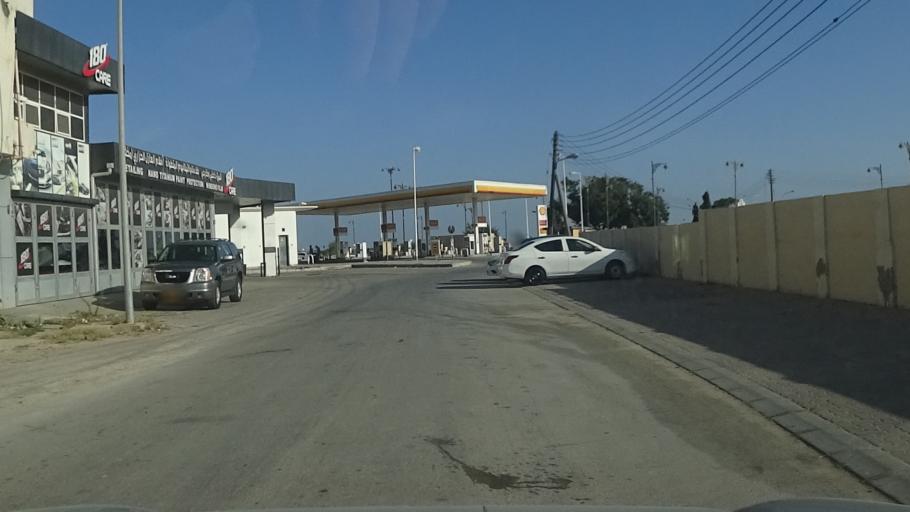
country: OM
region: Zufar
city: Salalah
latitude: 17.0271
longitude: 54.1707
